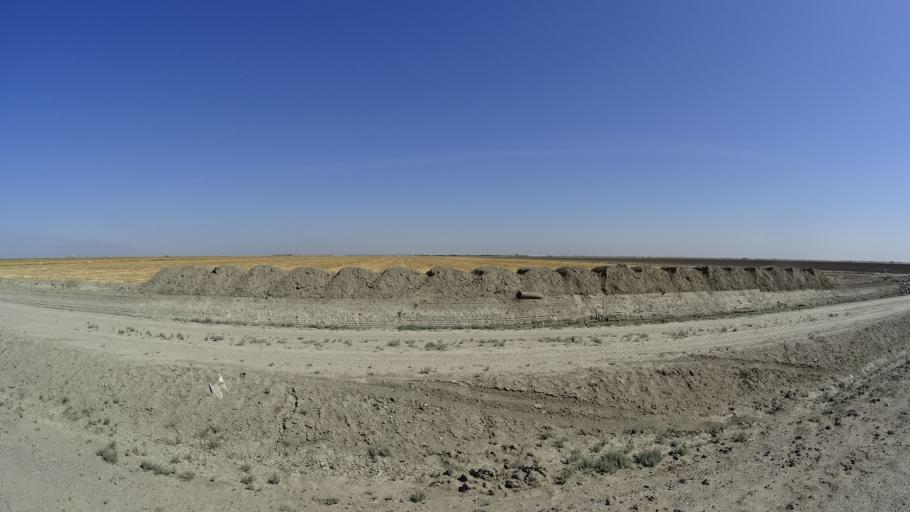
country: US
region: California
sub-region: Tulare County
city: Alpaugh
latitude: 35.9780
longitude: -119.5548
